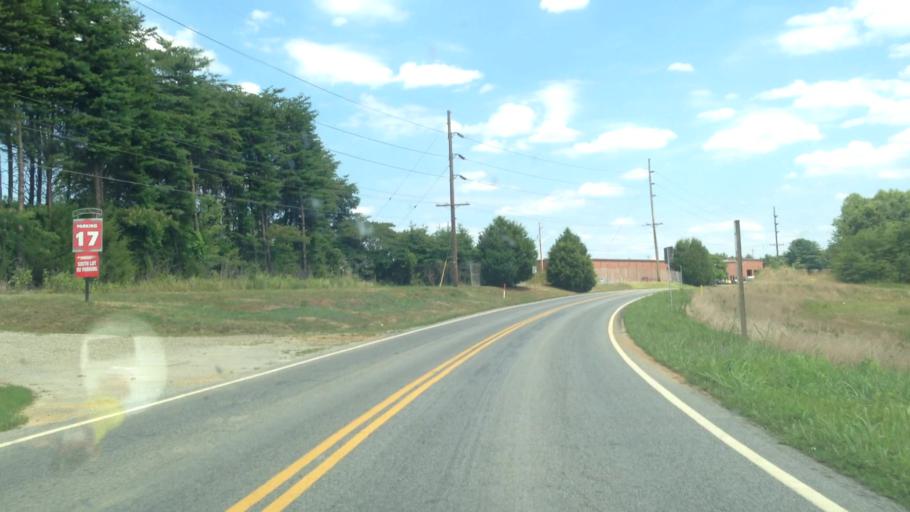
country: US
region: Virginia
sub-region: Henry County
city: Chatmoss
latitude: 36.6274
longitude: -79.8563
